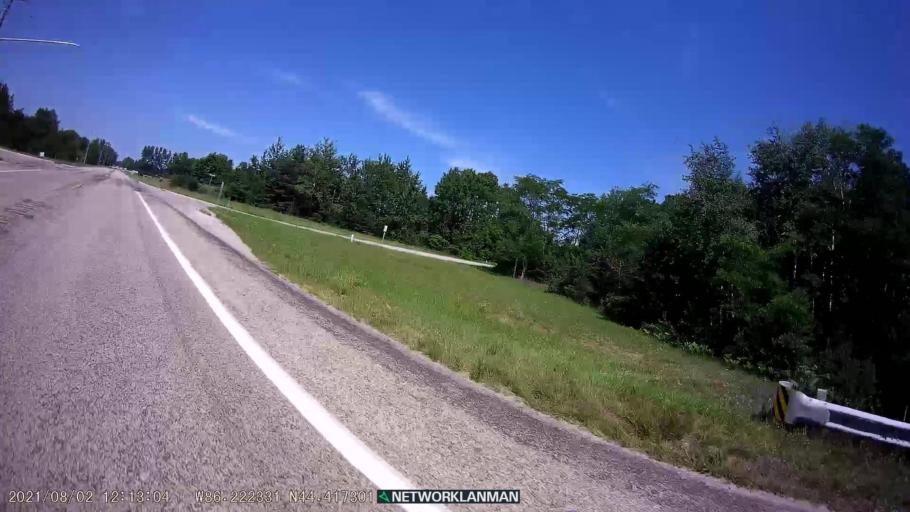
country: US
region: Michigan
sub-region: Manistee County
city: Manistee
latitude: 44.4181
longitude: -86.2223
